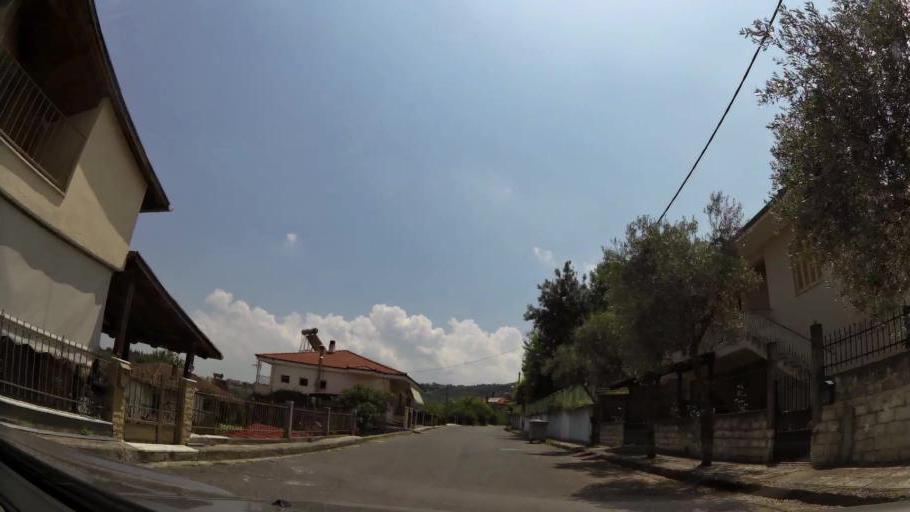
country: GR
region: Central Macedonia
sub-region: Nomos Imathias
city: Veroia
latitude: 40.5143
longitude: 22.1884
